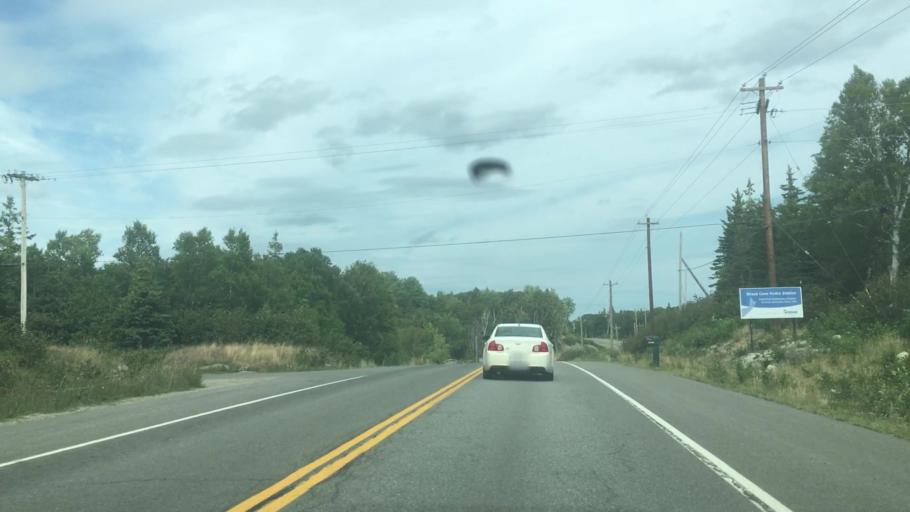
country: CA
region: Nova Scotia
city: Sydney Mines
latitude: 46.5207
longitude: -60.4226
